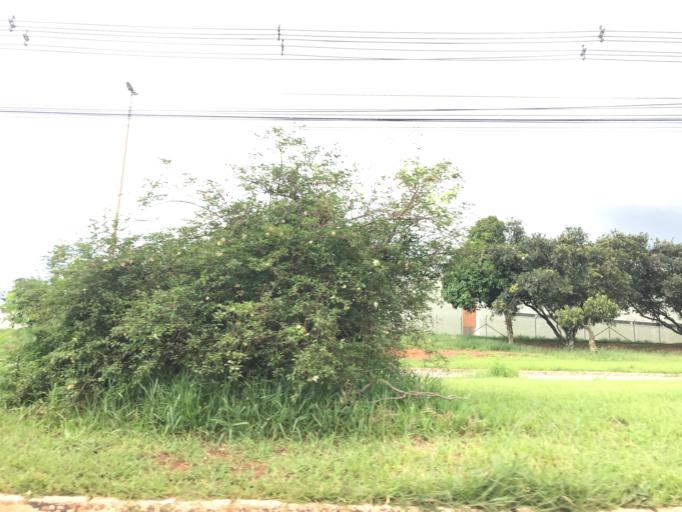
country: BR
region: Federal District
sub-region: Brasilia
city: Brasilia
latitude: -15.8294
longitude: -47.9370
